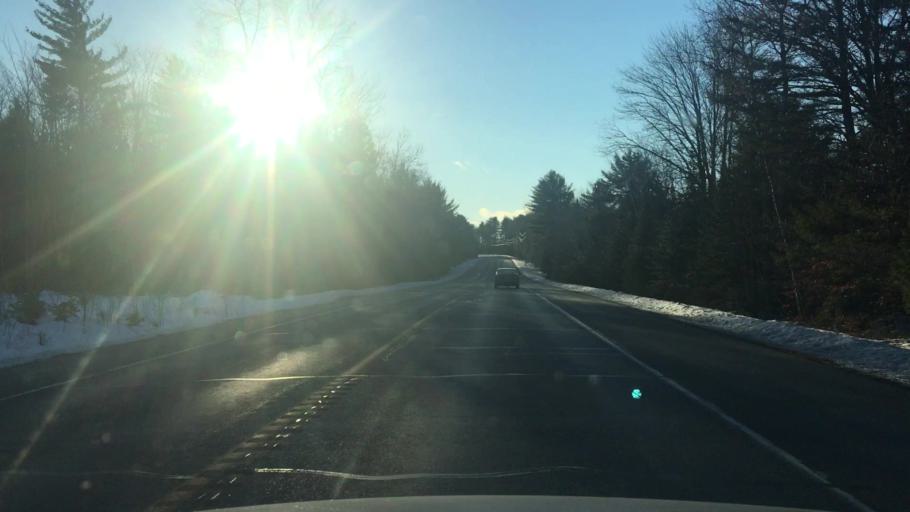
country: US
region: Maine
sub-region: Franklin County
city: New Sharon
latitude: 44.6691
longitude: -69.9456
